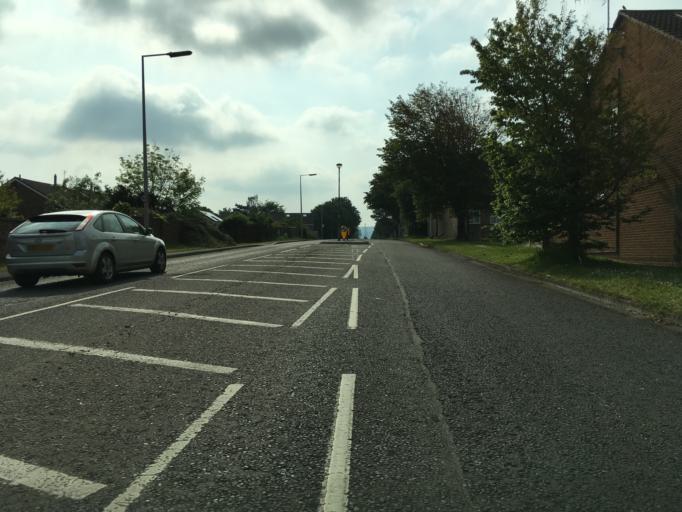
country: GB
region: England
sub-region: North Somerset
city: Nailsea
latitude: 51.4270
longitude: -2.7612
